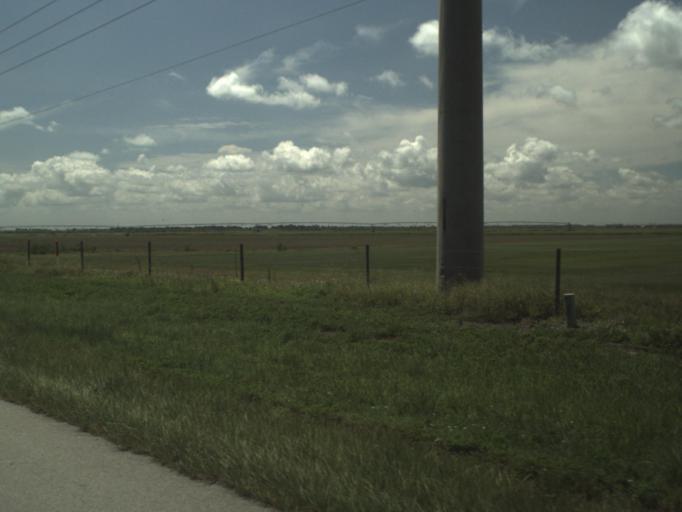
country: US
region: Florida
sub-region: Martin County
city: Indiantown
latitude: 27.0118
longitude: -80.5055
